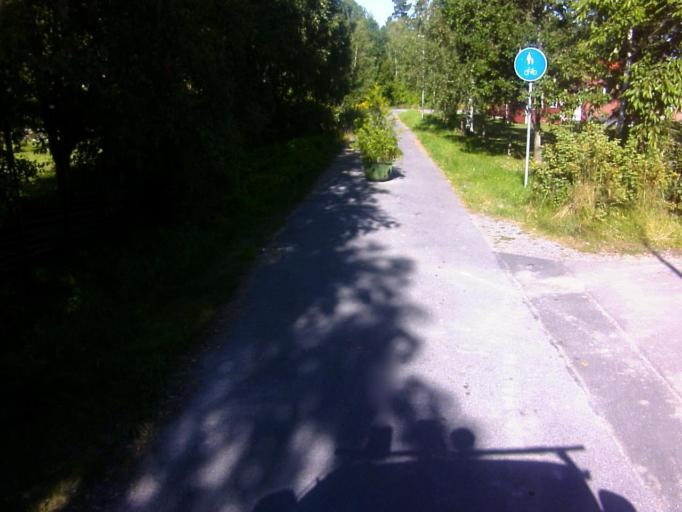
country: SE
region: Soedermanland
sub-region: Eskilstuna Kommun
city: Hallbybrunn
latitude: 59.3407
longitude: 16.4174
